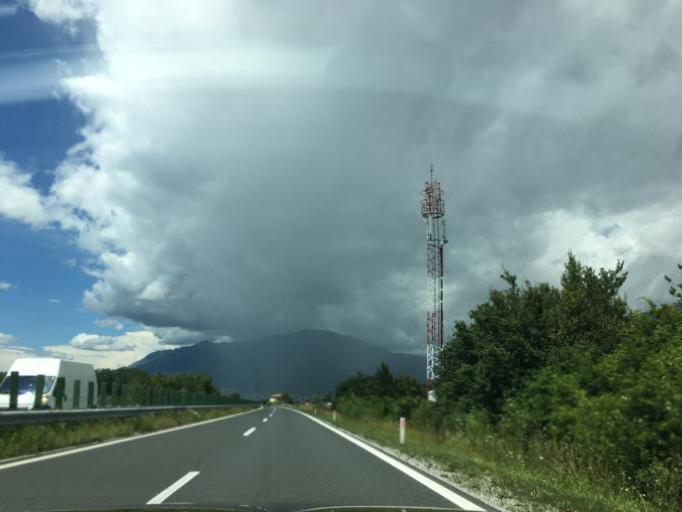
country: SI
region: Ajdovscina
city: Ajdovscina
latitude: 45.8674
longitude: 13.9317
